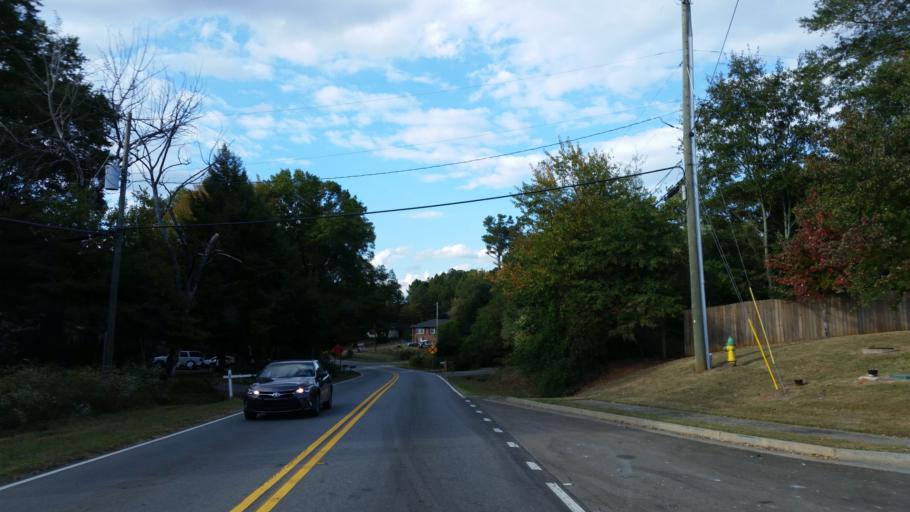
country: US
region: Georgia
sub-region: Bartow County
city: Cartersville
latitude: 34.2108
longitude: -84.8008
